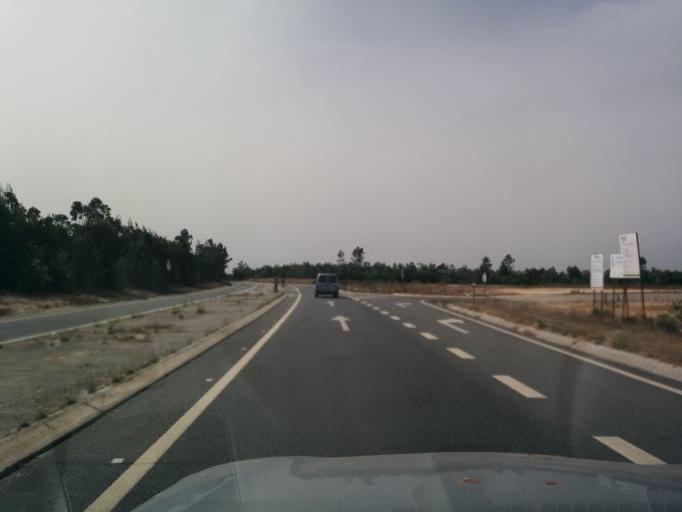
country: PT
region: Beja
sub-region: Odemira
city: Vila Nova de Milfontes
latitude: 37.6430
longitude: -8.7596
